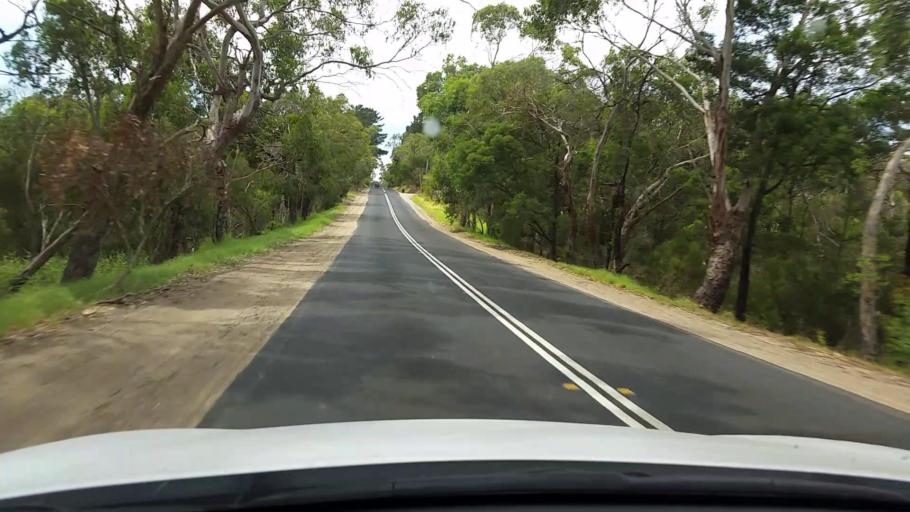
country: AU
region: Victoria
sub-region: Mornington Peninsula
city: Mount Martha
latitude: -38.2886
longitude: 145.0587
